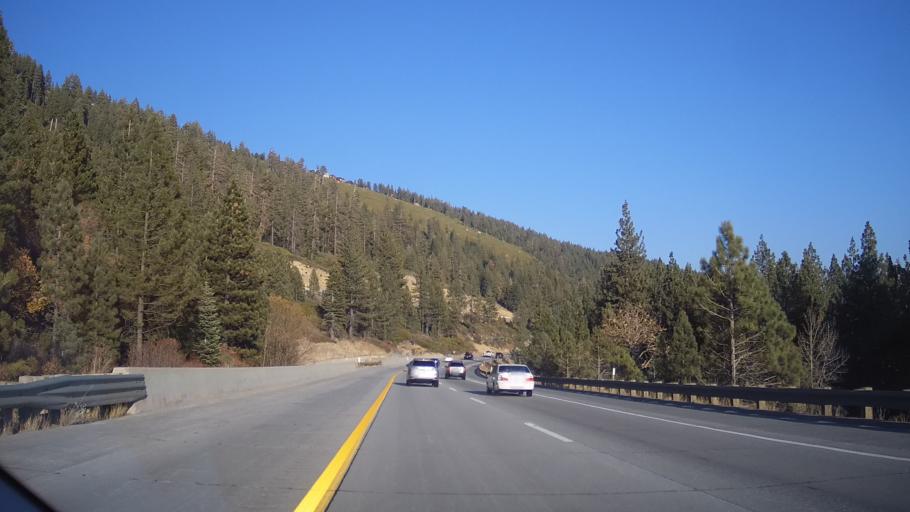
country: US
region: California
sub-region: Nevada County
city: Truckee
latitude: 39.3305
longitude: -120.2611
